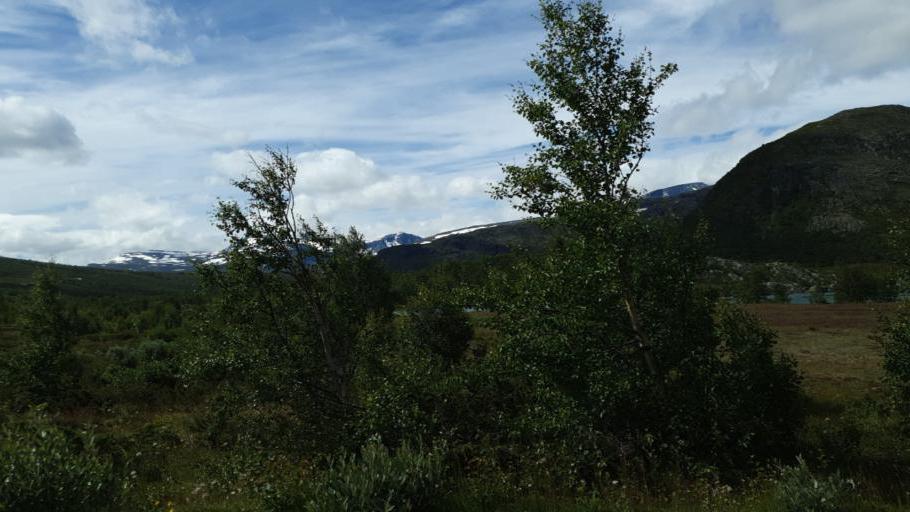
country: NO
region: Oppland
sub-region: Oystre Slidre
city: Heggenes
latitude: 61.4882
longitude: 8.8281
